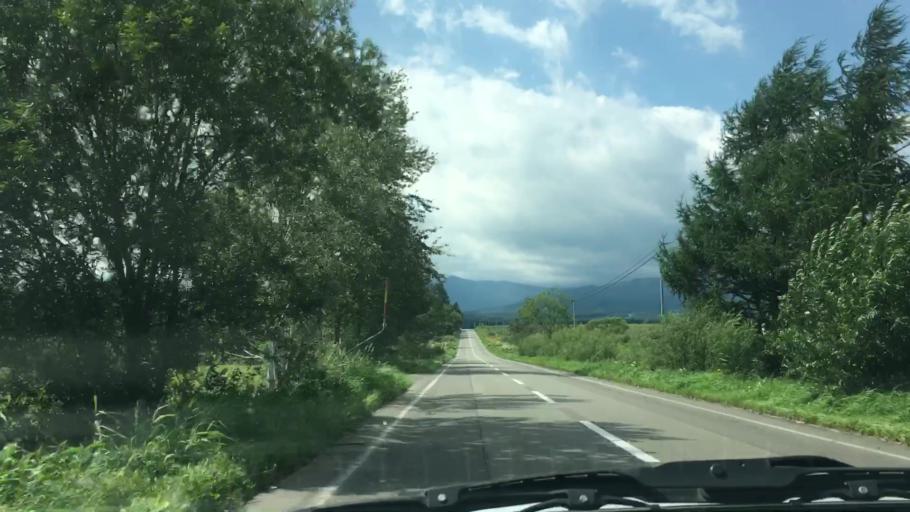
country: JP
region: Hokkaido
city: Otofuke
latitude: 43.2790
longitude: 143.3506
